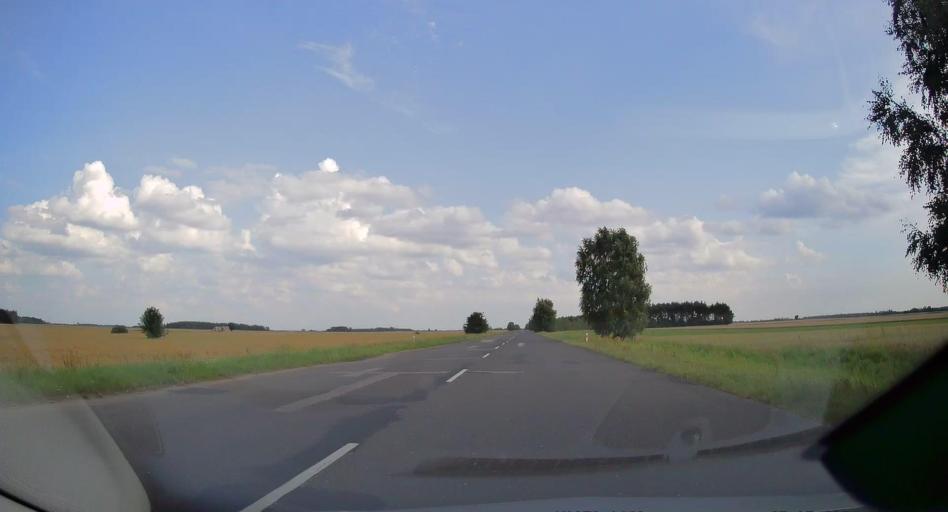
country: PL
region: Lodz Voivodeship
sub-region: Powiat tomaszowski
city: Rzeczyca
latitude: 51.6638
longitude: 20.2672
